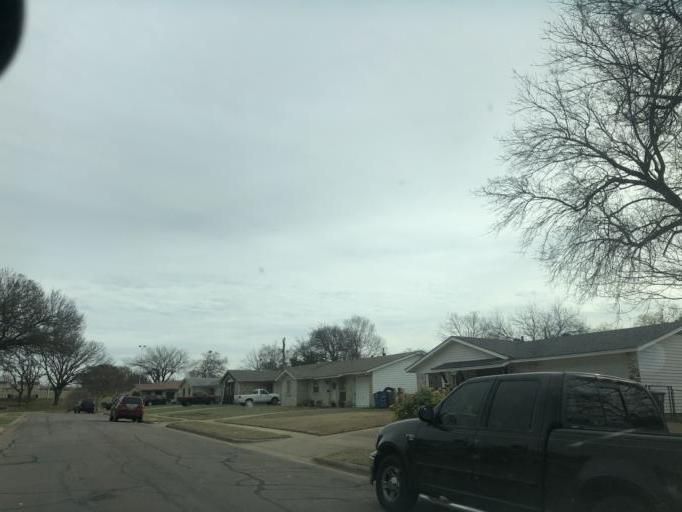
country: US
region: Texas
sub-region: Dallas County
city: Duncanville
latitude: 32.6659
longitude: -96.8338
